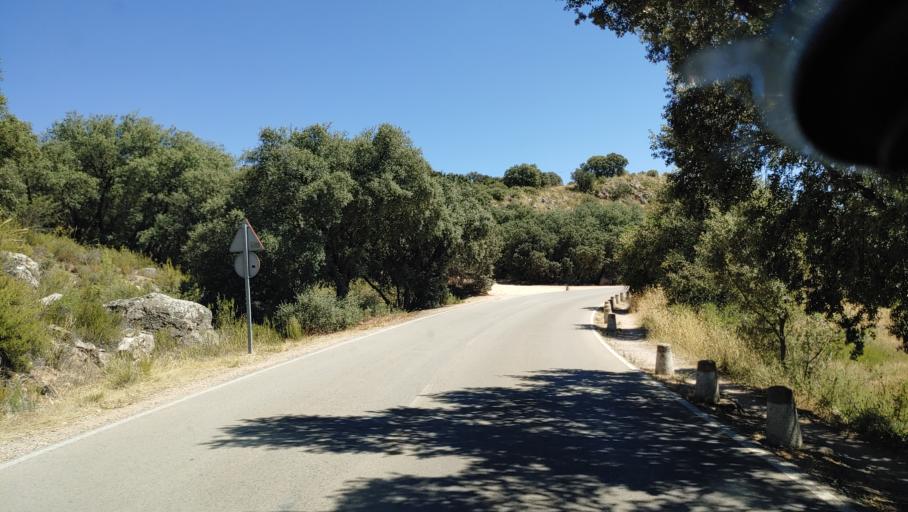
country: ES
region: Castille-La Mancha
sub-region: Provincia de Ciudad Real
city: Ruidera
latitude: 38.9600
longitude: -2.8714
